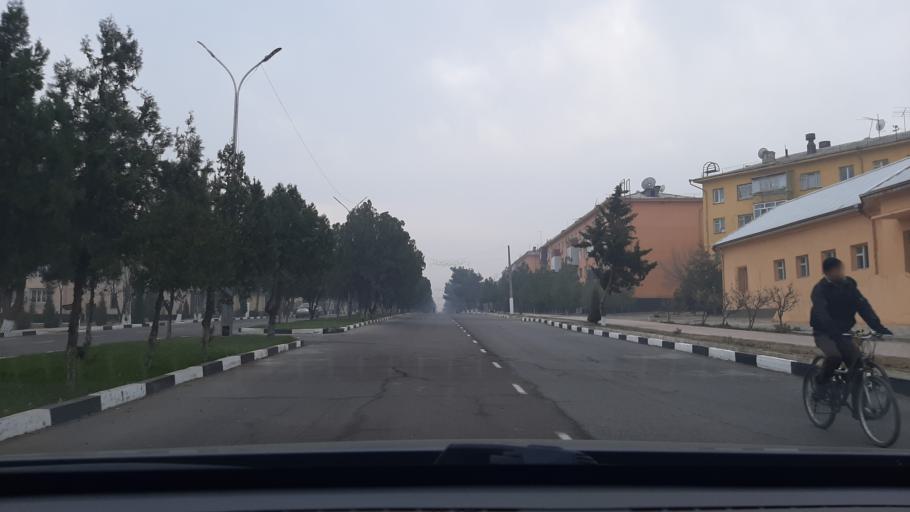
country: TJ
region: Viloyati Sughd
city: Chkalov
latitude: 40.2337
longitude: 69.6886
